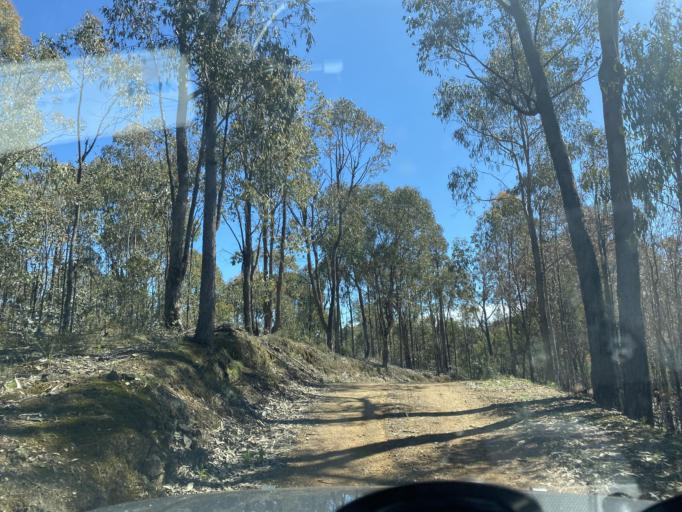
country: AU
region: Victoria
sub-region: Benalla
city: Benalla
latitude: -36.7324
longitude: 146.1828
